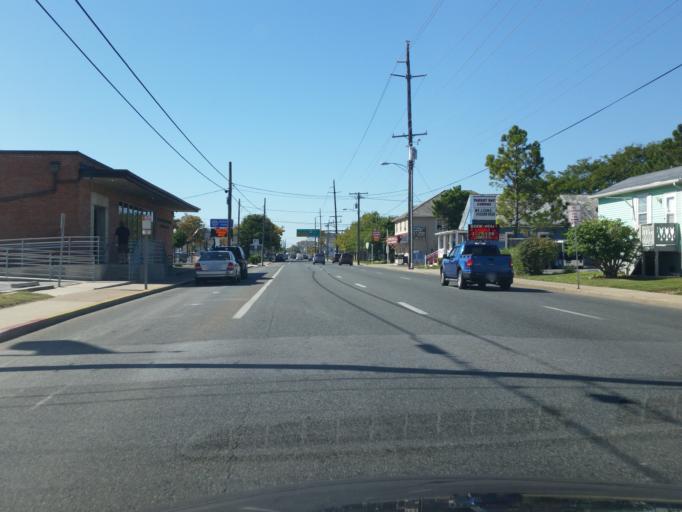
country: US
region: Maryland
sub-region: Worcester County
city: Ocean City
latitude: 38.3368
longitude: -75.0848
